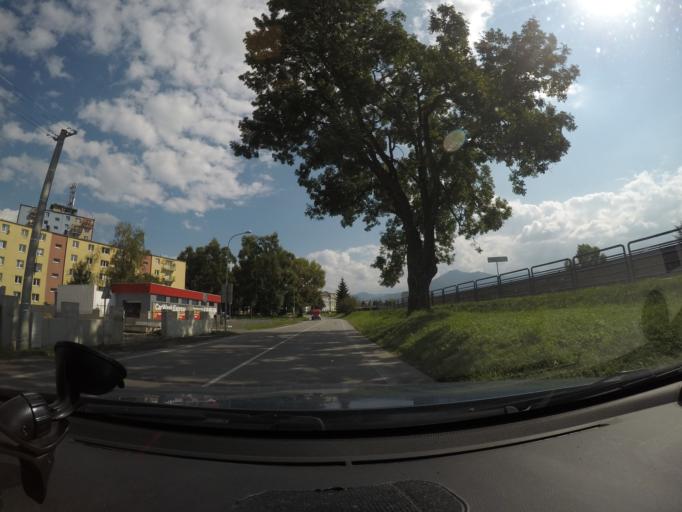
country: SK
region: Zilinsky
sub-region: Okres Liptovsky Mikulas
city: Liptovsky Mikulas
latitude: 49.0903
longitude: 19.6012
